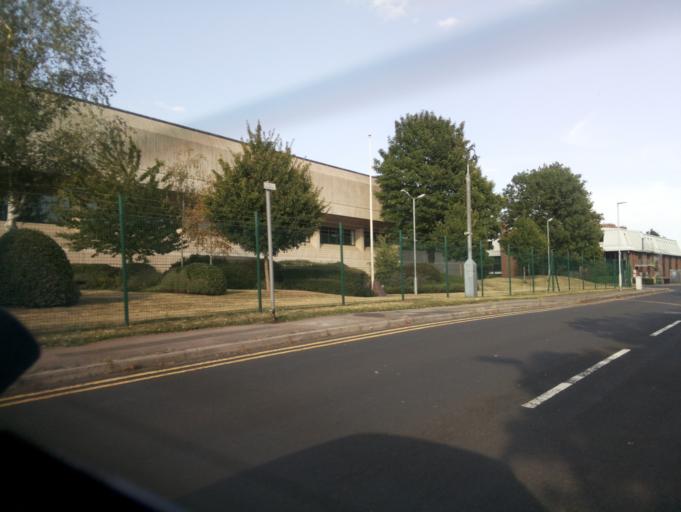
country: GB
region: England
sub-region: Gloucestershire
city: Barnwood
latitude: 51.8629
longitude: -2.1996
